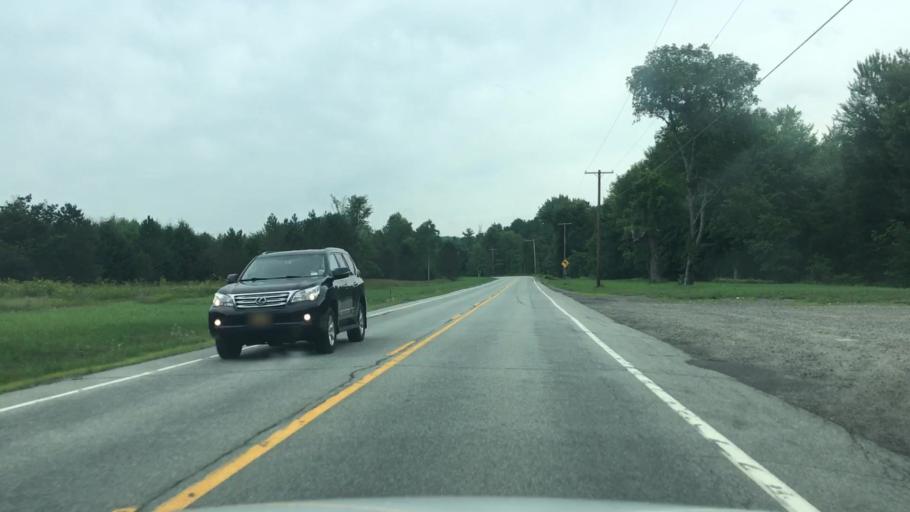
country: US
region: New York
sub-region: Essex County
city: Elizabethtown
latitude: 44.4061
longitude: -73.6946
